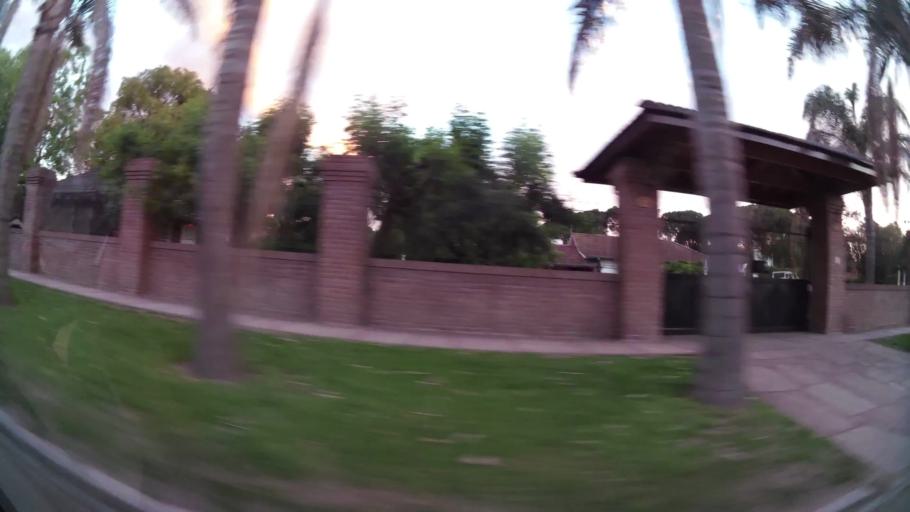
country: AR
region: Buenos Aires
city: Santa Catalina - Dique Lujan
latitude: -34.4748
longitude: -58.7667
